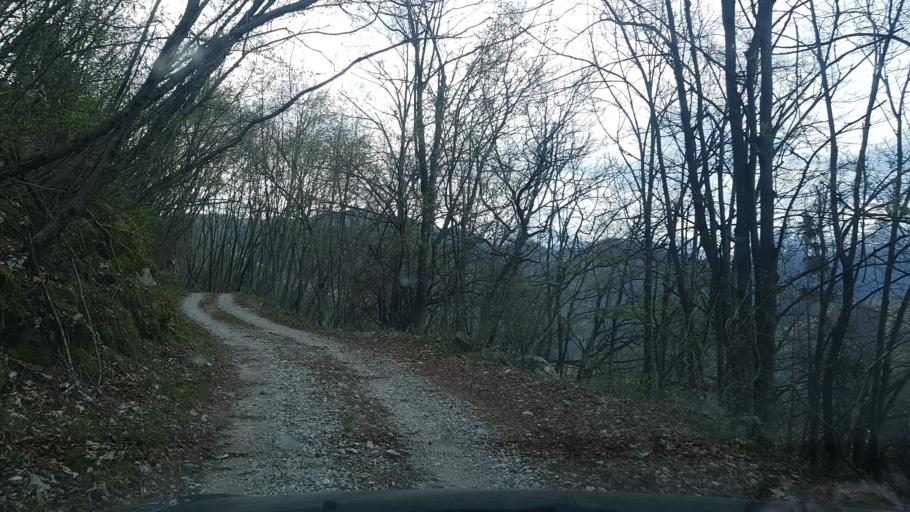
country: IT
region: Friuli Venezia Giulia
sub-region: Provincia di Udine
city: Trasaghis
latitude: 46.2865
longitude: 13.0373
